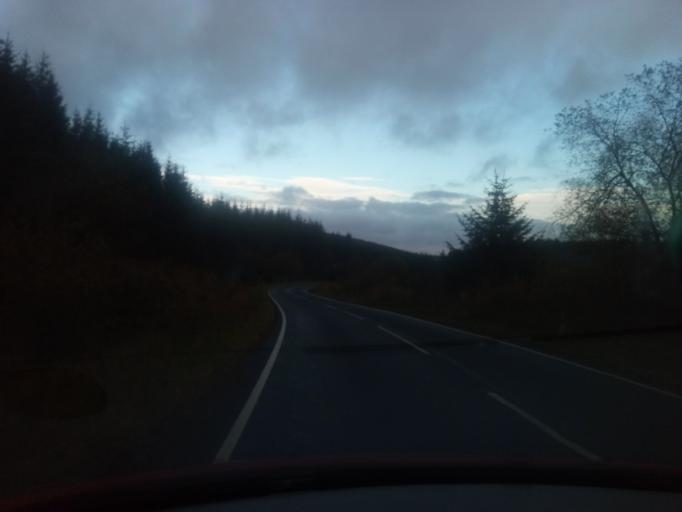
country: GB
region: Scotland
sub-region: The Scottish Borders
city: Hawick
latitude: 55.3284
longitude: -2.6483
